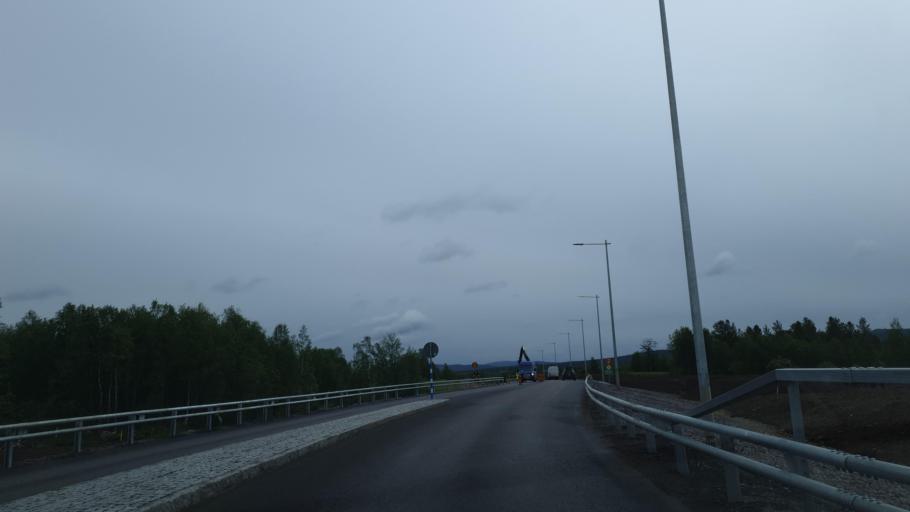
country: SE
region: Norrbotten
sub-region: Kiruna Kommun
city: Kiruna
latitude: 67.8475
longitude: 20.3197
